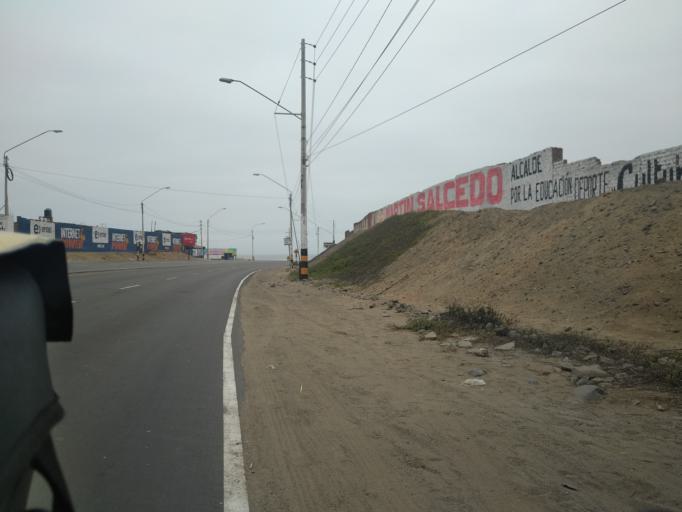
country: PE
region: La Libertad
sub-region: Provincia de Trujillo
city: Huanchaco
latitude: -8.0969
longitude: -79.1099
